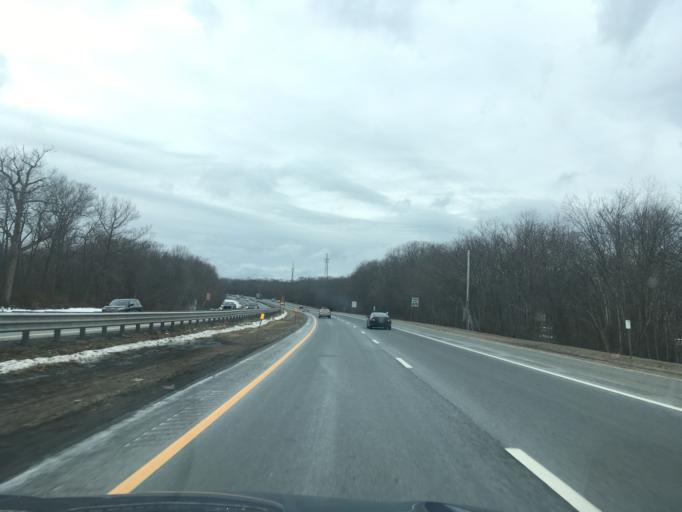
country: US
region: Rhode Island
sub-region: Kent County
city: West Warwick
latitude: 41.6663
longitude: -71.5099
